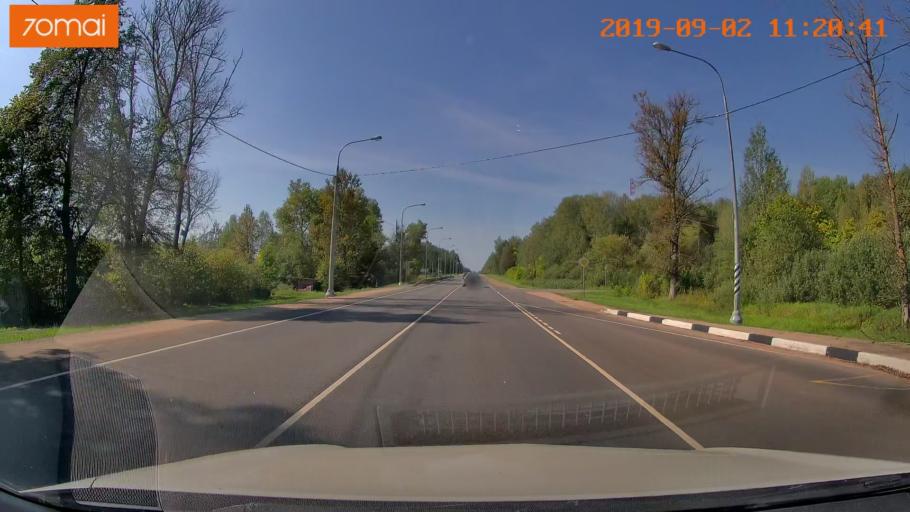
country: RU
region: Smolensk
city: Roslavl'
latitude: 54.0405
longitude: 33.0498
